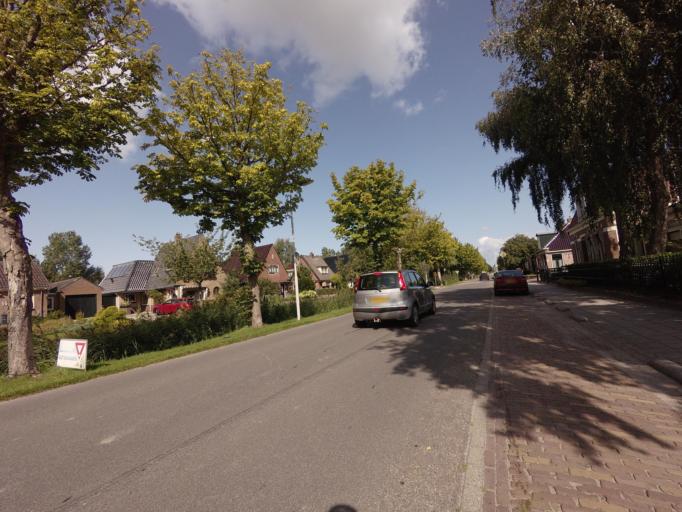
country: NL
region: Friesland
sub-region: Gemeente Het Bildt
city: Sint Annaparochie
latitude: 53.2789
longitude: 5.6567
